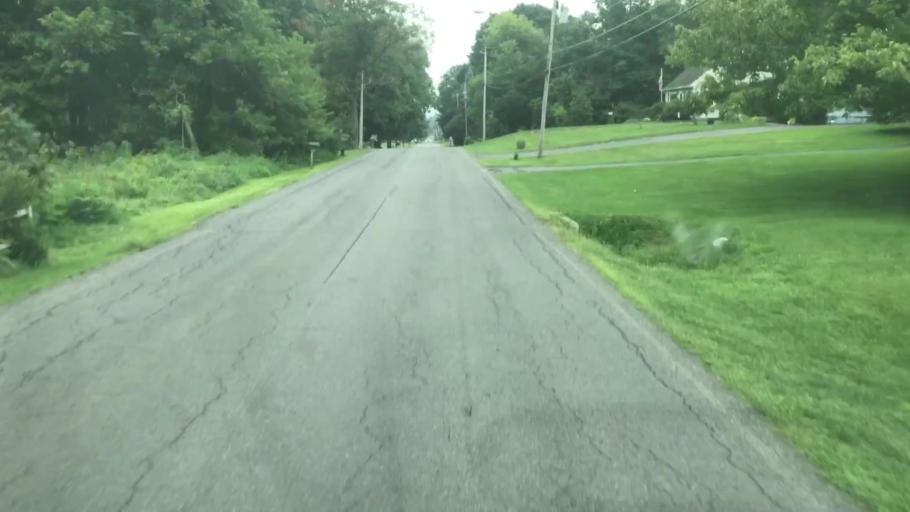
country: US
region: New York
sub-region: Onondaga County
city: Skaneateles
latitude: 42.9508
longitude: -76.4490
